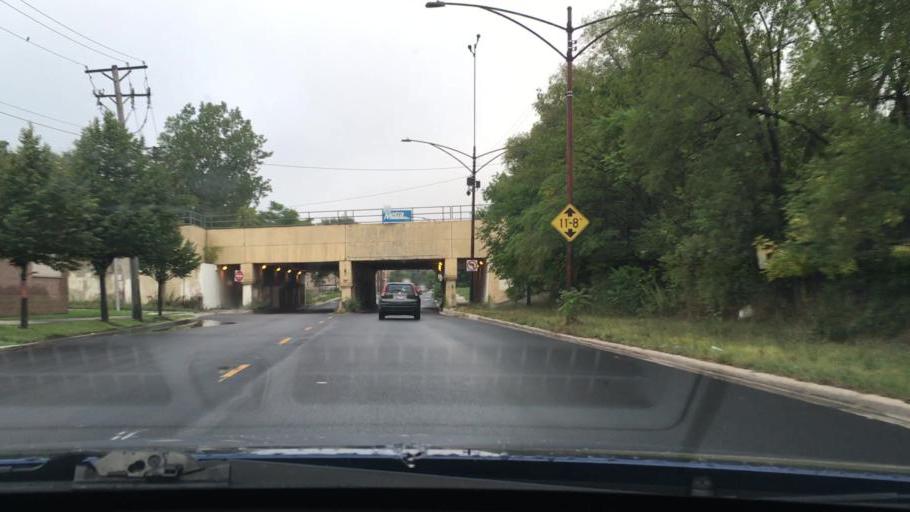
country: US
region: Illinois
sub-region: Cook County
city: Evergreen Park
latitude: 41.7434
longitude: -87.6412
